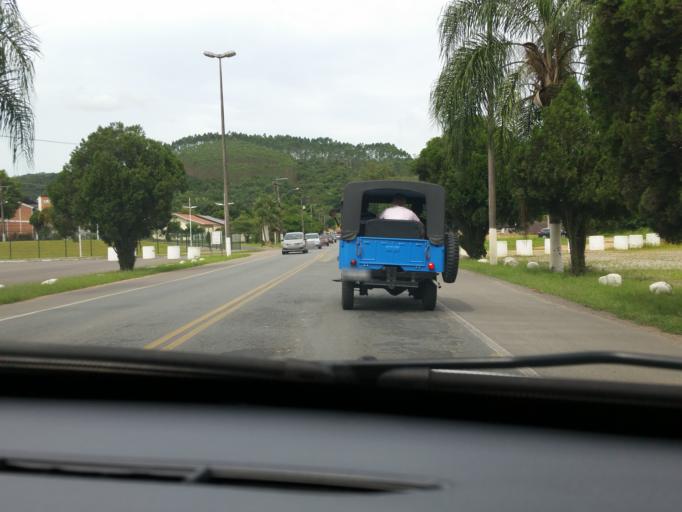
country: BR
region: Santa Catarina
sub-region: Rodeio
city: Gavea
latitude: -27.0259
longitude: -49.3767
